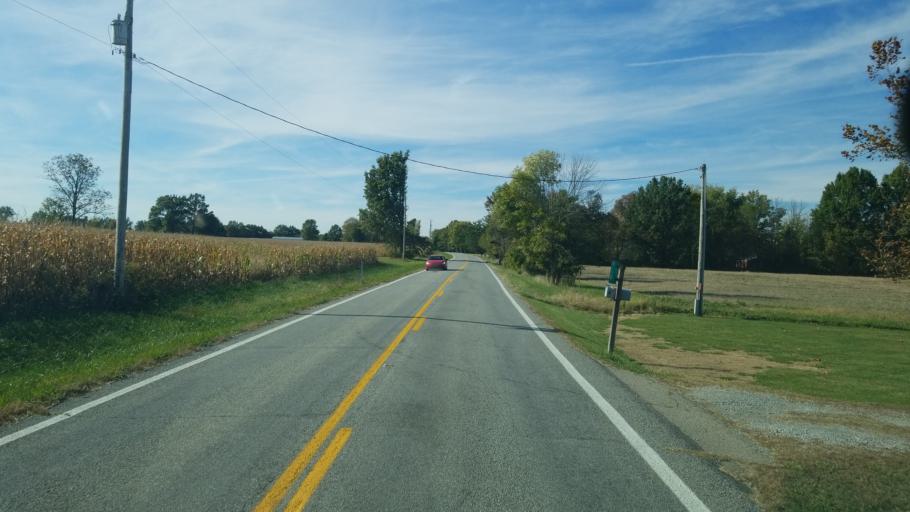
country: US
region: Ohio
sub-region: Warren County
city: Morrow
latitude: 39.4048
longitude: -84.0515
